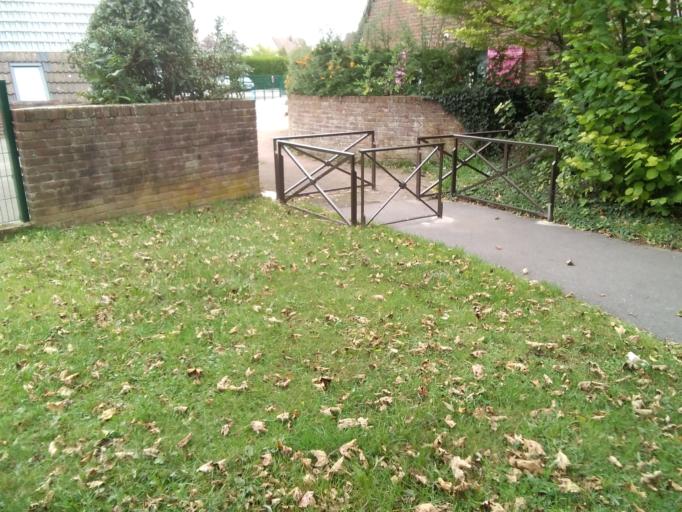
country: FR
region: Picardie
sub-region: Departement de la Somme
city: Amiens
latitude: 49.9218
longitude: 2.2979
